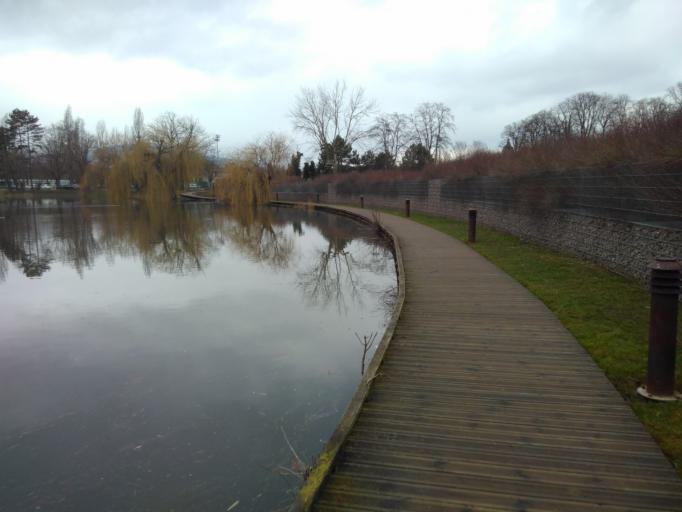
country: FR
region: Alsace
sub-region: Departement du Bas-Rhin
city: Selestat
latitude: 48.2538
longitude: 7.4519
